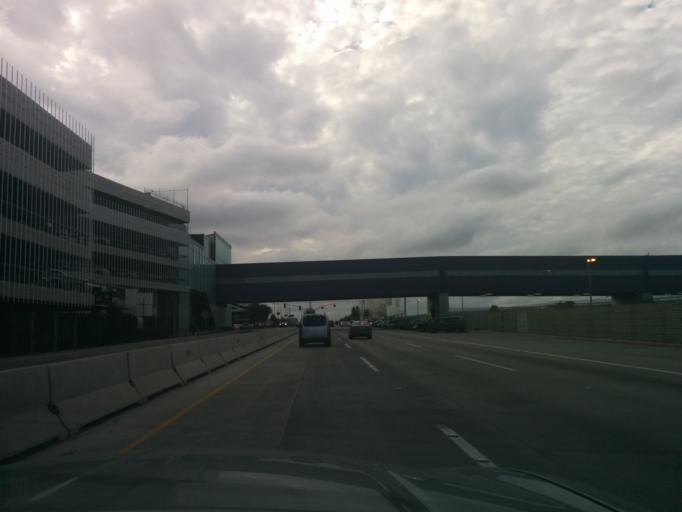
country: MX
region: Baja California
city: Tijuana
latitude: 32.5471
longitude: -116.9737
